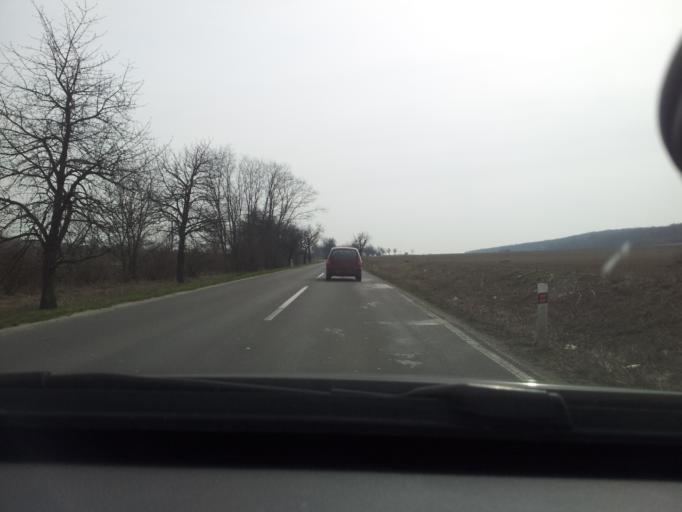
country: SK
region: Trnavsky
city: Hlohovec
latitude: 48.4116
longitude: 17.8361
